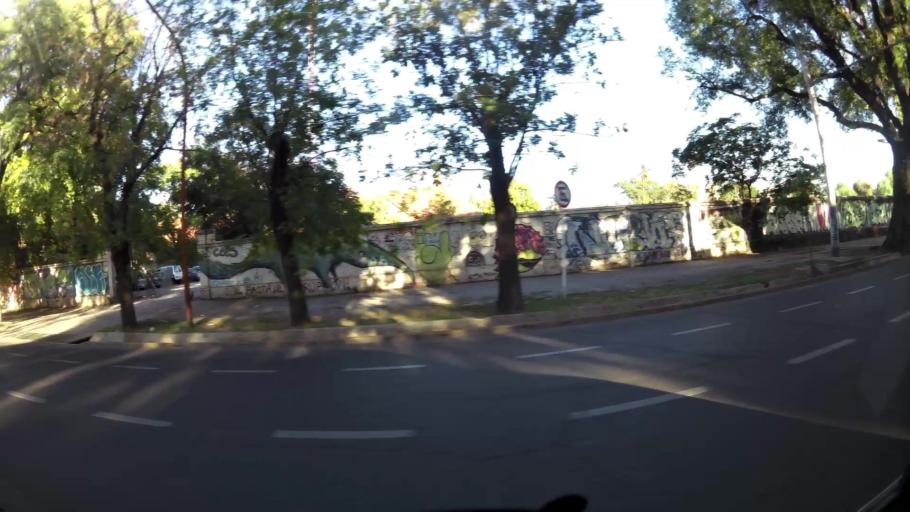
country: AR
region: Mendoza
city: Mendoza
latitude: -32.8838
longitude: -68.8470
